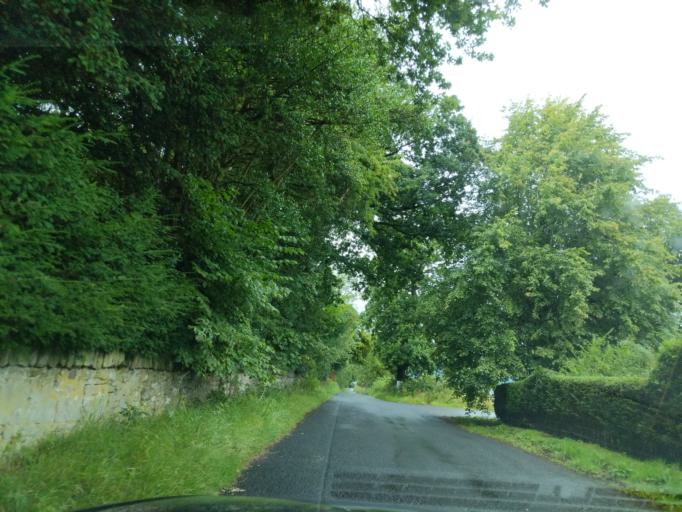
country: GB
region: Scotland
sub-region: West Lothian
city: Broxburn
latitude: 55.9824
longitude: -3.4639
